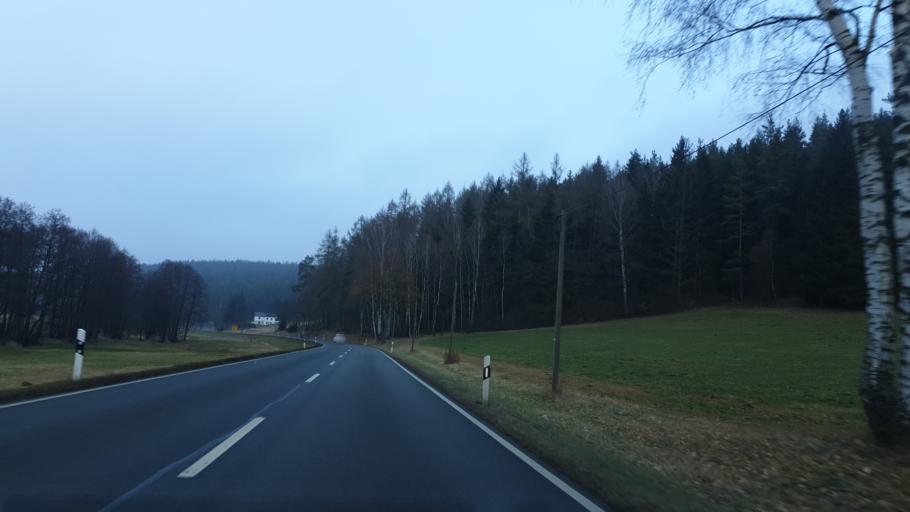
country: DE
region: Saxony
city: Bad Brambach
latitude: 50.2629
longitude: 12.3009
